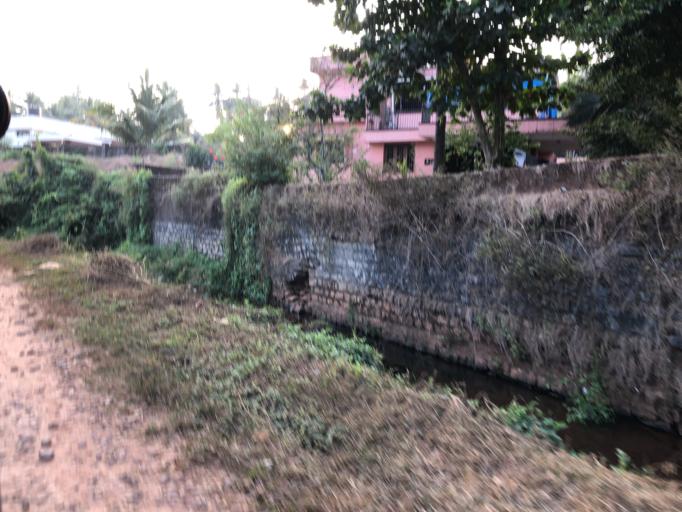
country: IN
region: Karnataka
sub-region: Dakshina Kannada
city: Mangalore
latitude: 12.8984
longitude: 74.8656
